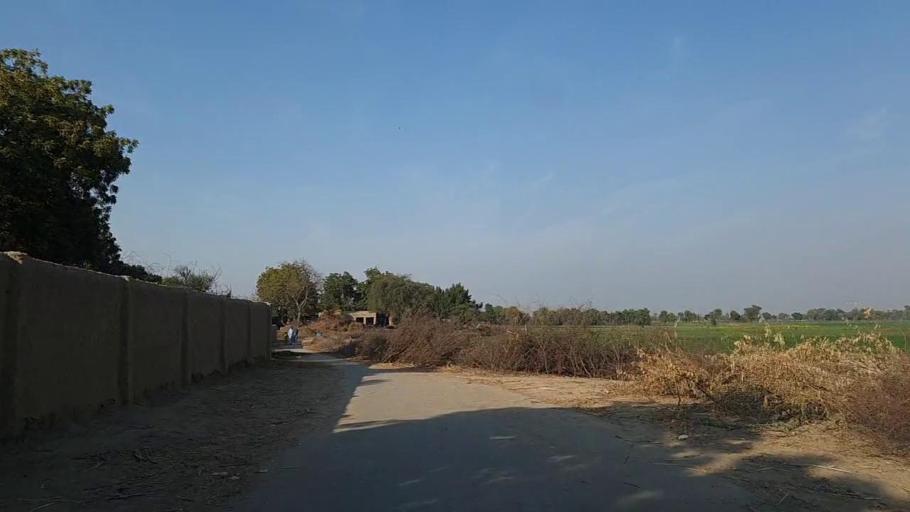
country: PK
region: Sindh
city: Nawabshah
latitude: 26.3752
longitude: 68.4772
